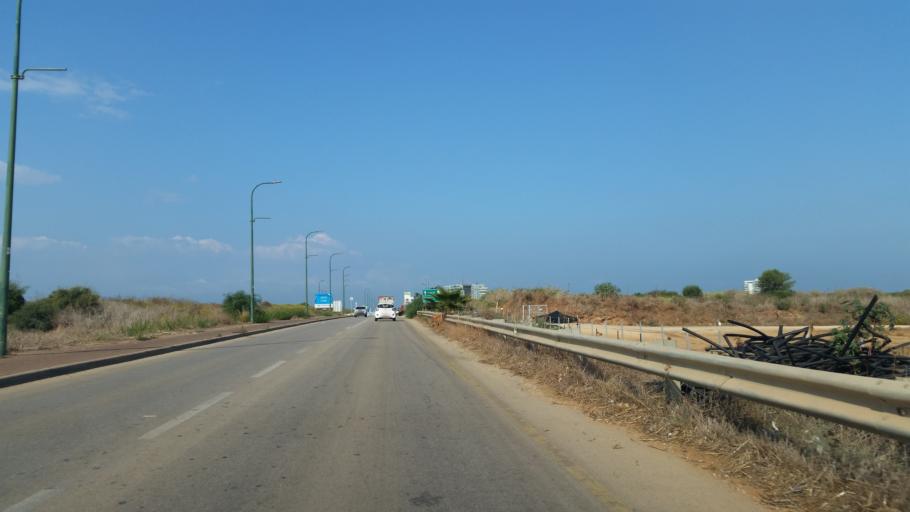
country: IL
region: Tel Aviv
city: Herzliya Pituah
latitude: 32.1545
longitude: 34.8040
